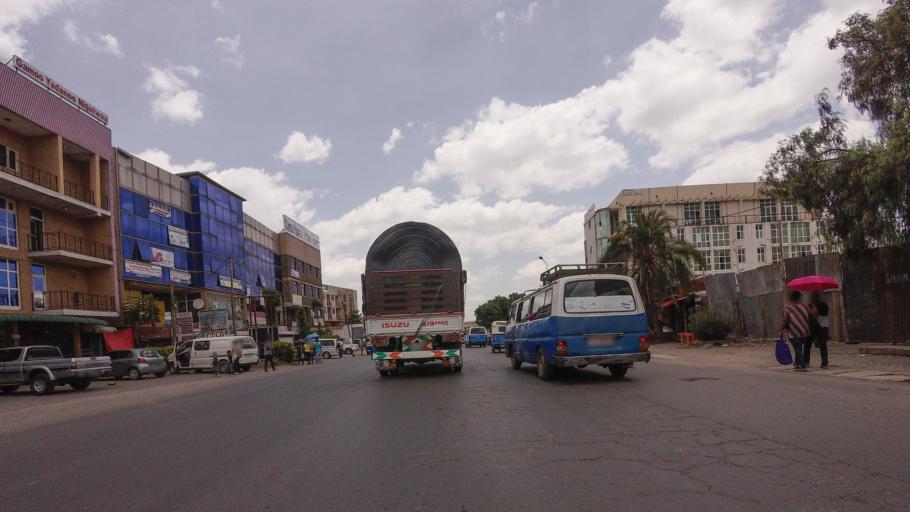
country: ET
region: Oromiya
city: Bishoftu
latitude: 8.7512
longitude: 38.9656
